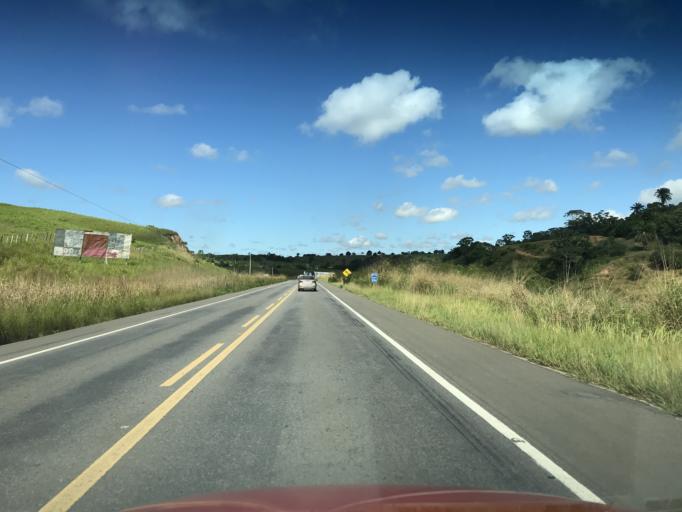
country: BR
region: Bahia
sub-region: Conceicao Do Almeida
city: Muritiba
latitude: -12.9294
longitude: -39.2529
